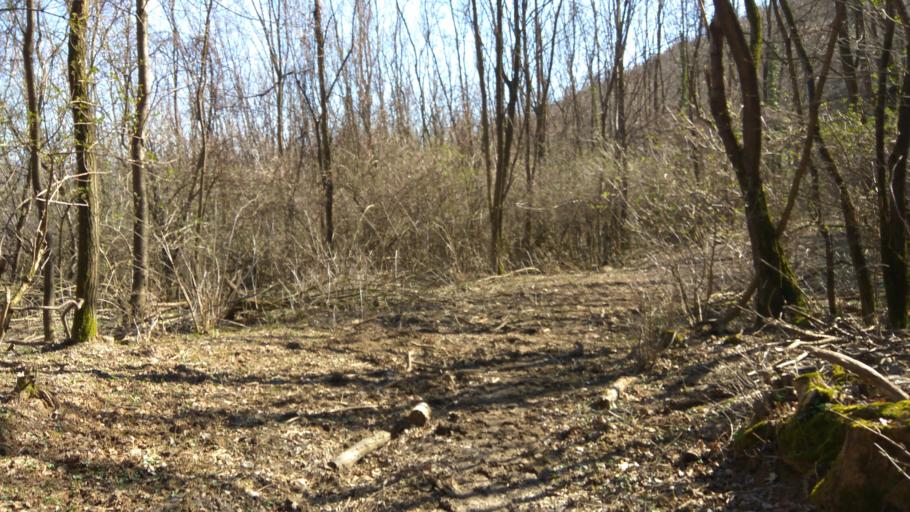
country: HU
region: Pest
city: Csobanka
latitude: 47.6351
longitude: 18.9827
